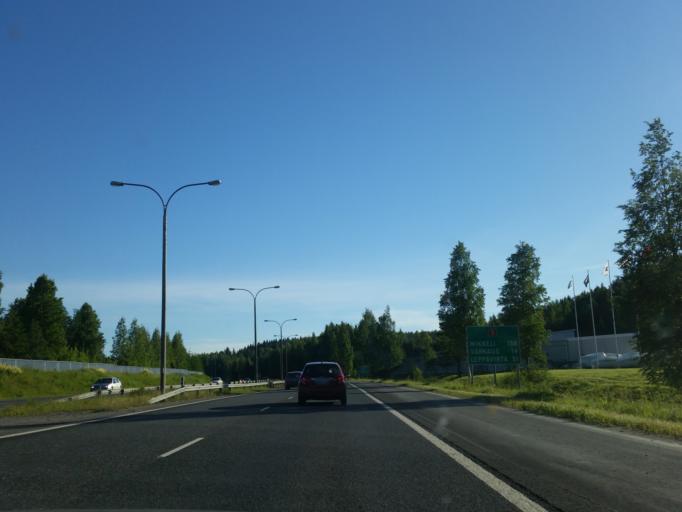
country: FI
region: Northern Savo
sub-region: Kuopio
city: Kuopio
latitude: 62.8788
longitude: 27.6282
